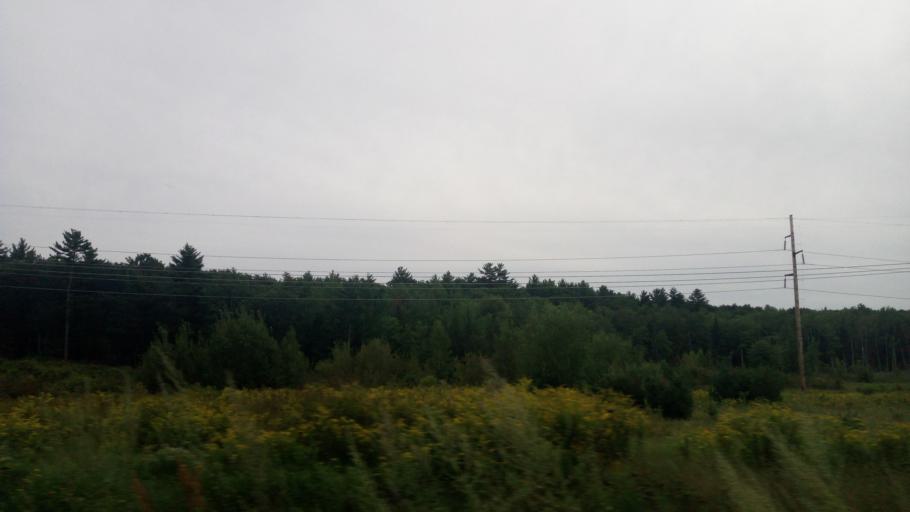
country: US
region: Maine
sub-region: Kennebec County
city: Chelsea
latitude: 44.2736
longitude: -69.6654
